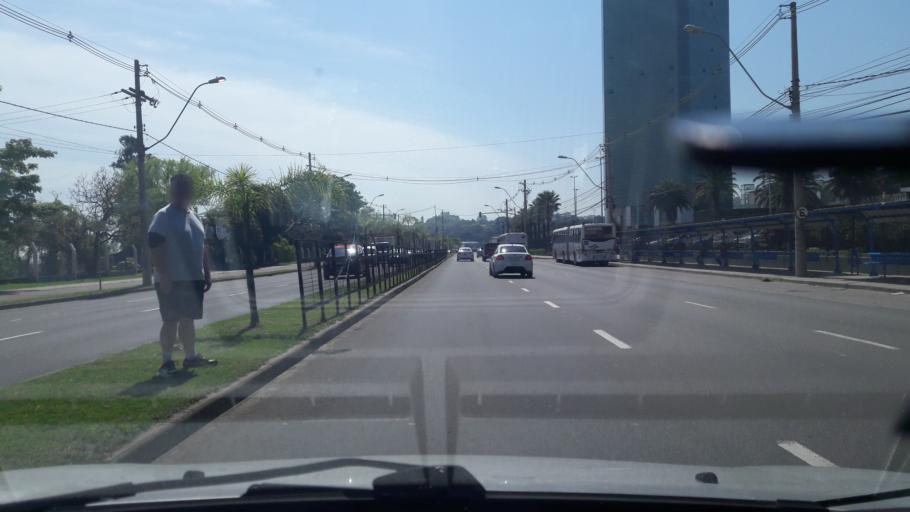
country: BR
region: Rio Grande do Sul
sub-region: Porto Alegre
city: Porto Alegre
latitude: -30.0862
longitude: -51.2477
